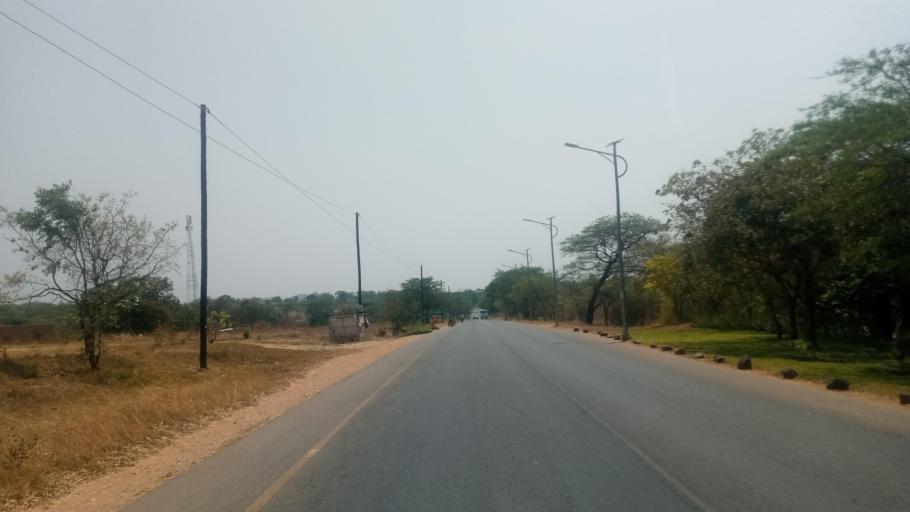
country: ZM
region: Lusaka
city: Lusaka
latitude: -15.4626
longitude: 28.4337
